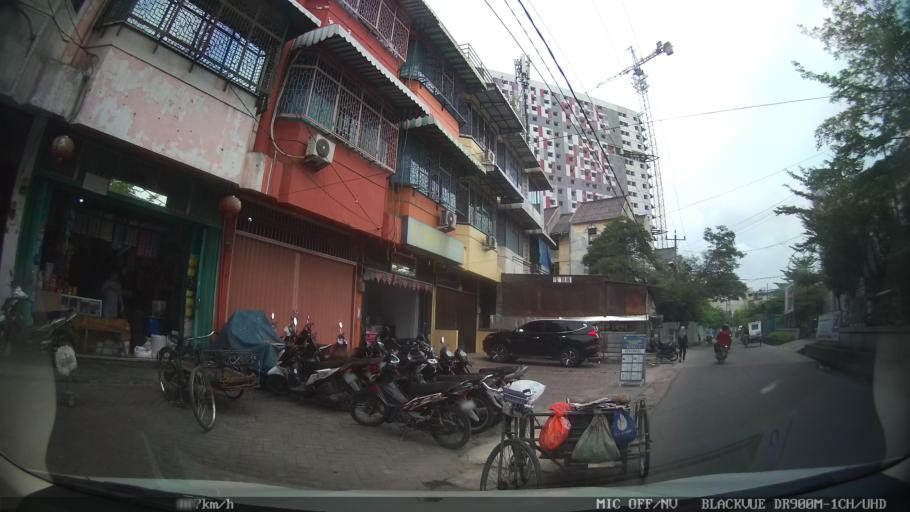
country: ID
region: North Sumatra
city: Medan
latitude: 3.5856
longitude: 98.7048
